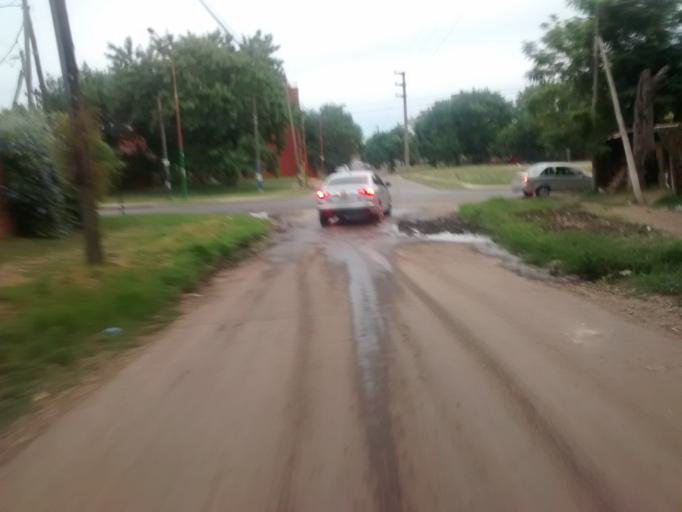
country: AR
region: Buenos Aires
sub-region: Partido de La Plata
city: La Plata
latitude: -34.9446
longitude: -57.9236
